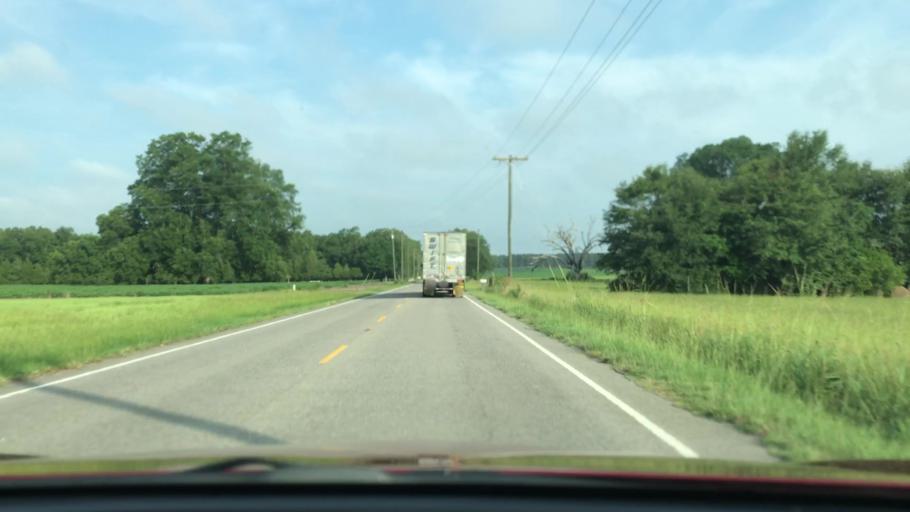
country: US
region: South Carolina
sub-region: Barnwell County
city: Blackville
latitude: 33.6087
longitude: -81.2721
